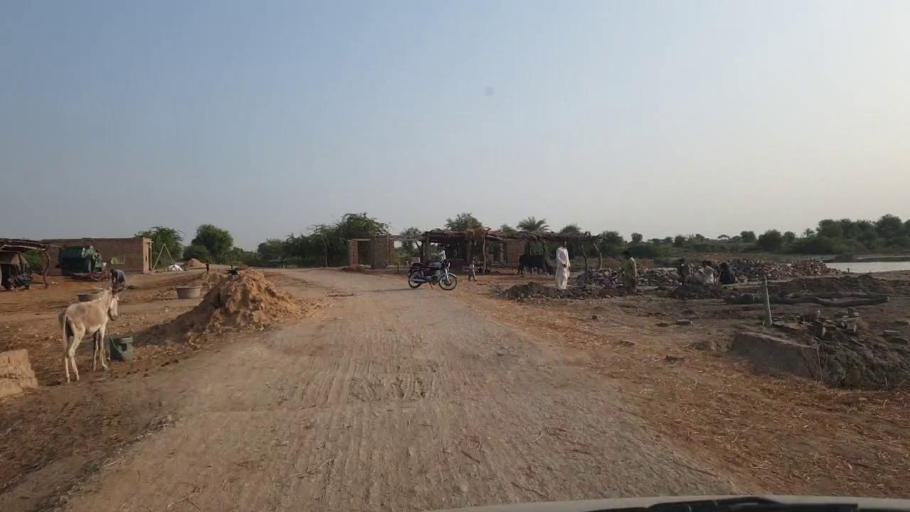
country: PK
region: Sindh
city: Rajo Khanani
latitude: 25.0172
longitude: 68.7848
